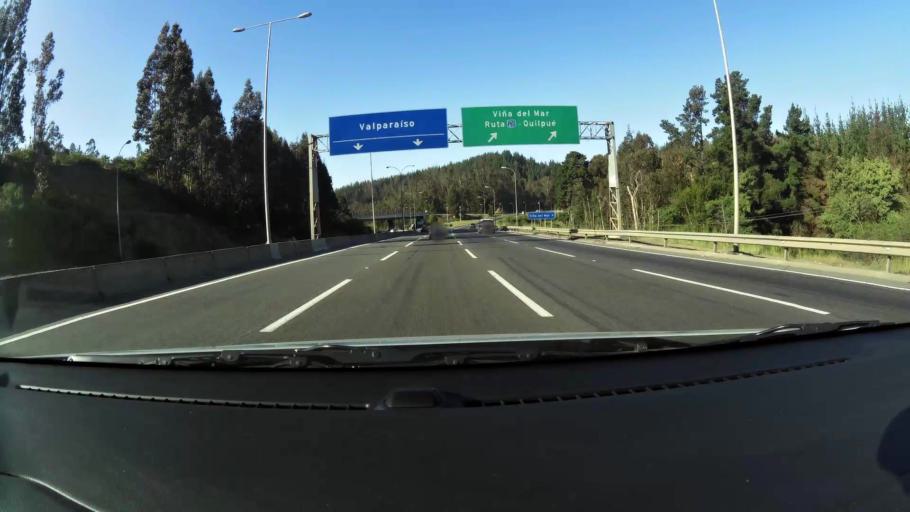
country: CL
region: Valparaiso
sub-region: Provincia de Valparaiso
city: Vina del Mar
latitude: -33.0991
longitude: -71.5476
